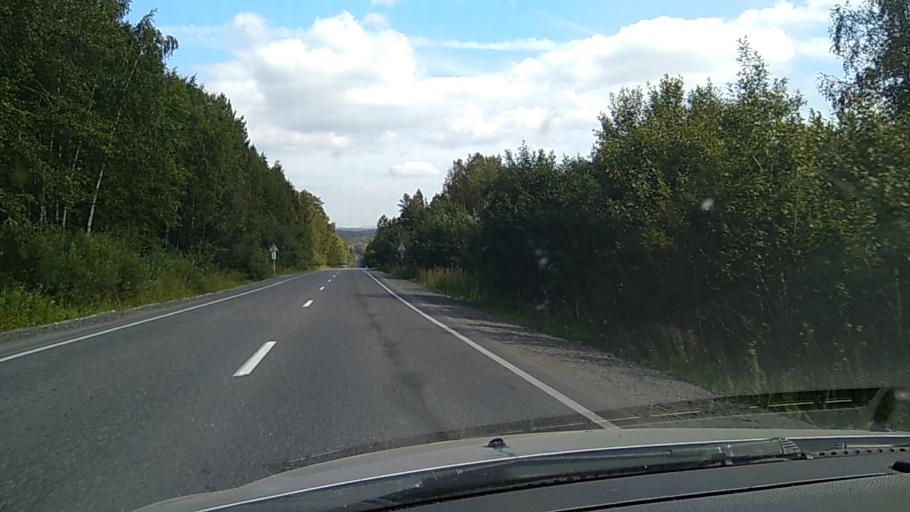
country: RU
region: Chelyabinsk
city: Syrostan
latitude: 55.1204
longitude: 59.8226
